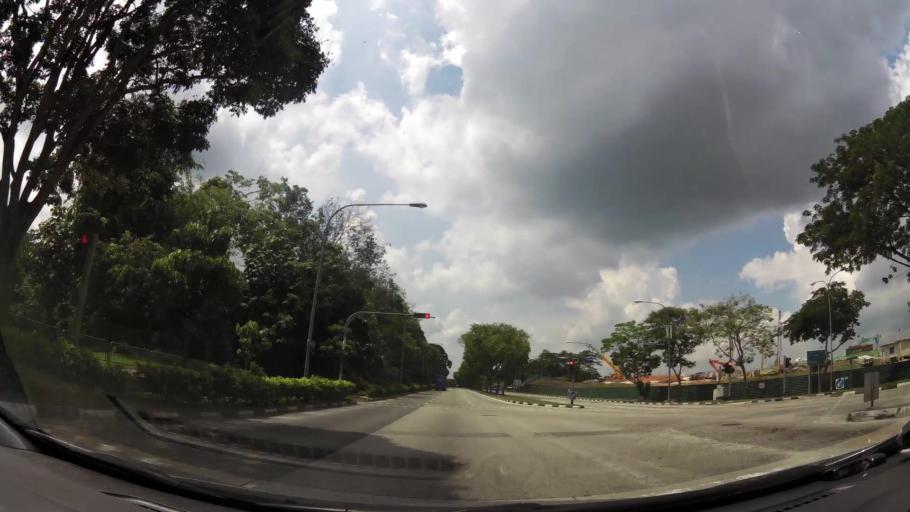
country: MY
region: Johor
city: Johor Bahru
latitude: 1.4159
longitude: 103.8012
